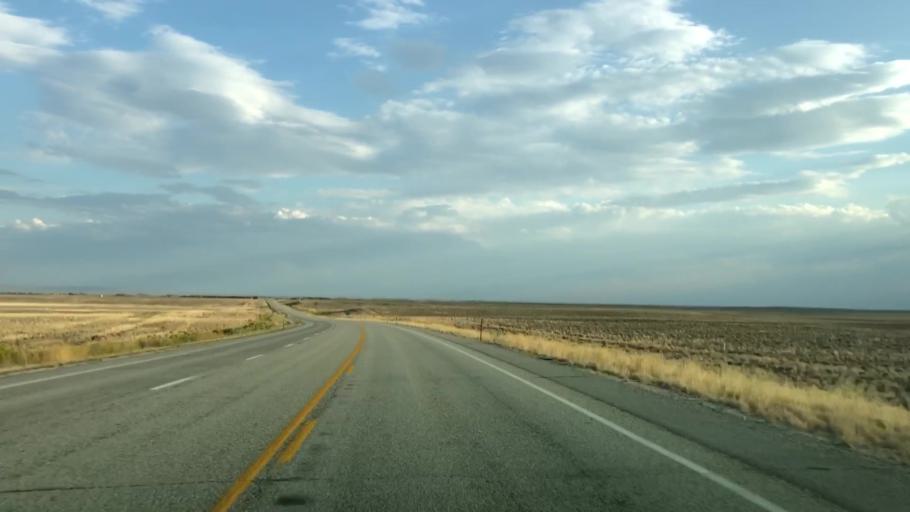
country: US
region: Wyoming
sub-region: Sweetwater County
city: North Rock Springs
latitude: 42.1904
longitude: -109.4806
